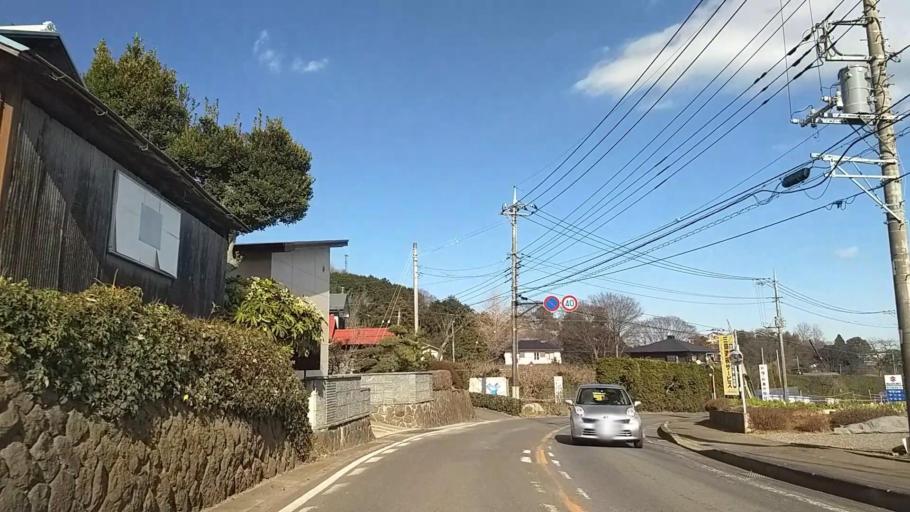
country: JP
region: Kanagawa
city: Isehara
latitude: 35.4188
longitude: 139.2881
